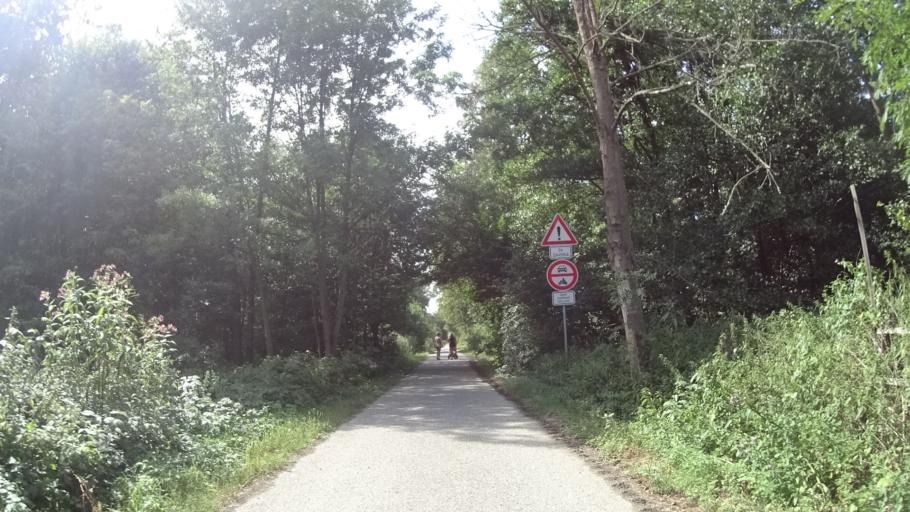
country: CZ
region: Olomoucky
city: Naklo
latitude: 49.6825
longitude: 17.1427
